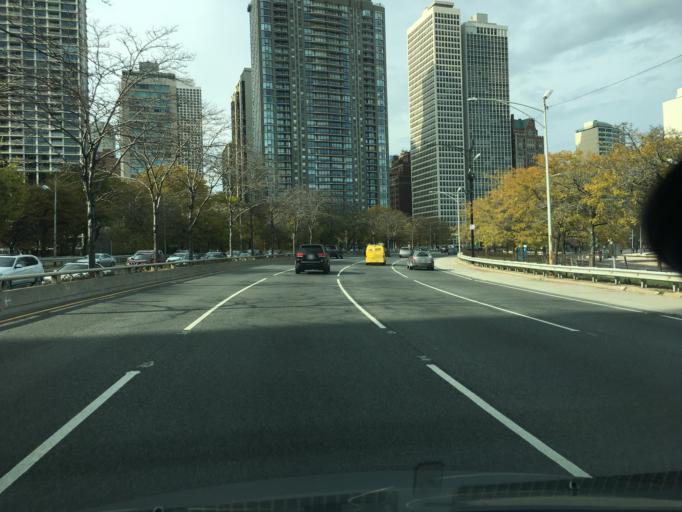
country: US
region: Illinois
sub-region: Cook County
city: Chicago
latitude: 41.9013
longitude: -87.6216
